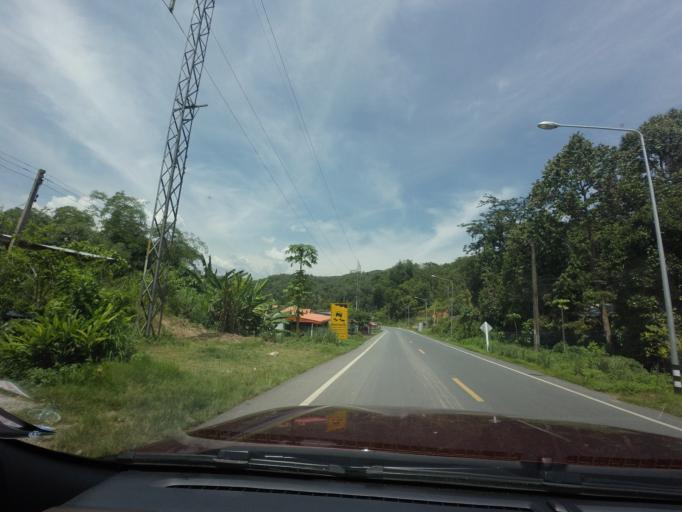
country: TH
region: Yala
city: Betong
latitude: 5.9193
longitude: 101.1681
